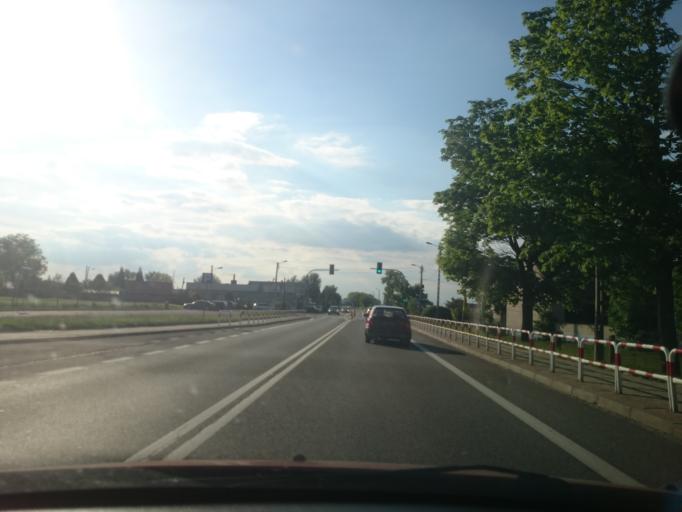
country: PL
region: Opole Voivodeship
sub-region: Powiat strzelecki
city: Izbicko
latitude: 50.5524
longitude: 18.2228
